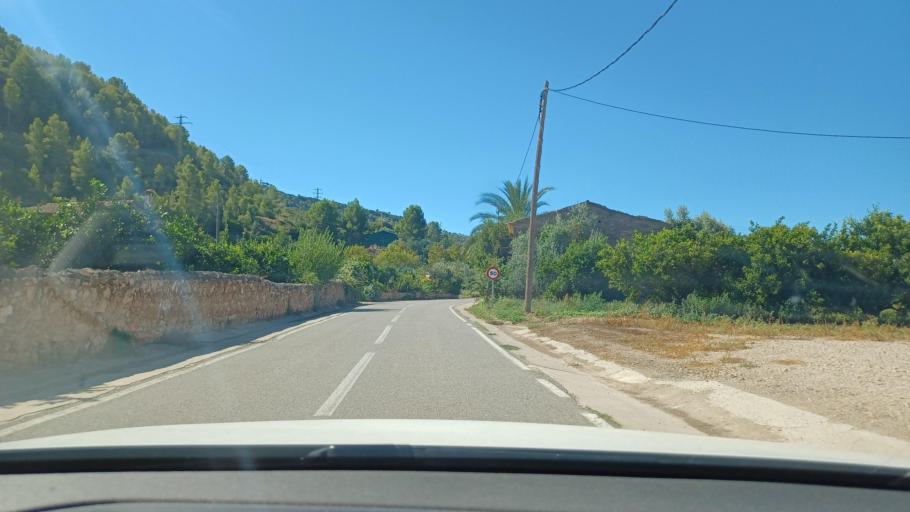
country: ES
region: Catalonia
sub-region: Provincia de Tarragona
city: Benifallet
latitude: 40.9706
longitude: 0.5155
